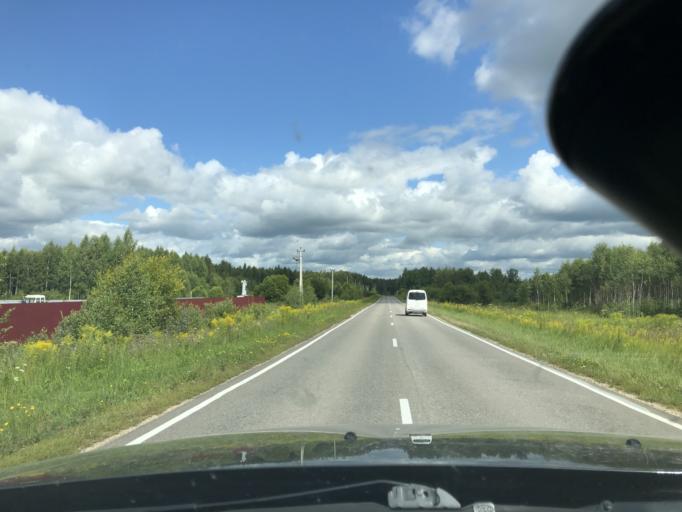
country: RU
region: Tula
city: Revyakino
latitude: 54.4173
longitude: 37.6922
